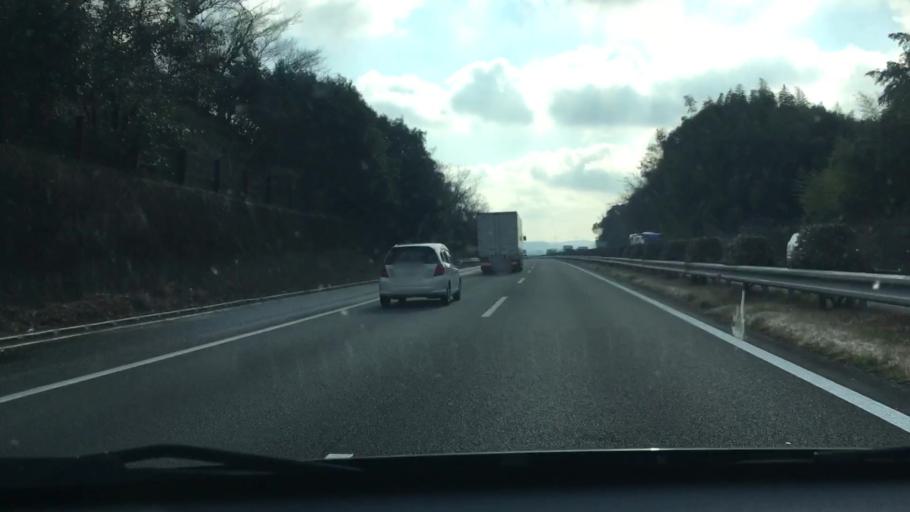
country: JP
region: Kumamoto
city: Kumamoto
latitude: 32.7256
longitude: 130.7723
